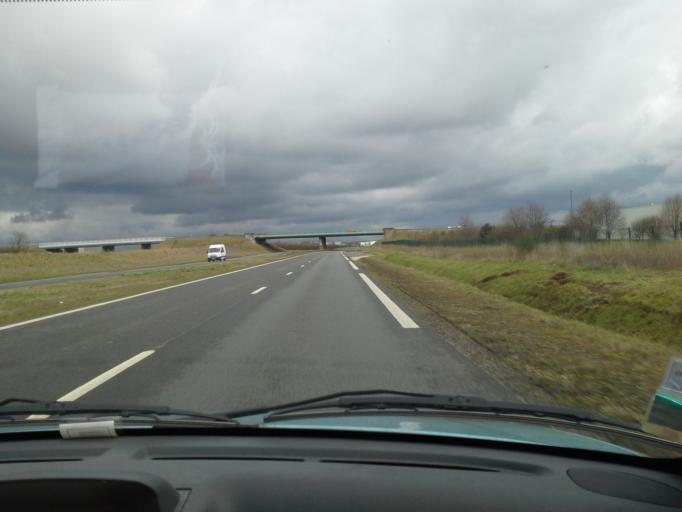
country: FR
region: Centre
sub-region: Departement du Loir-et-Cher
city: Villebarou
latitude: 47.6169
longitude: 1.3240
